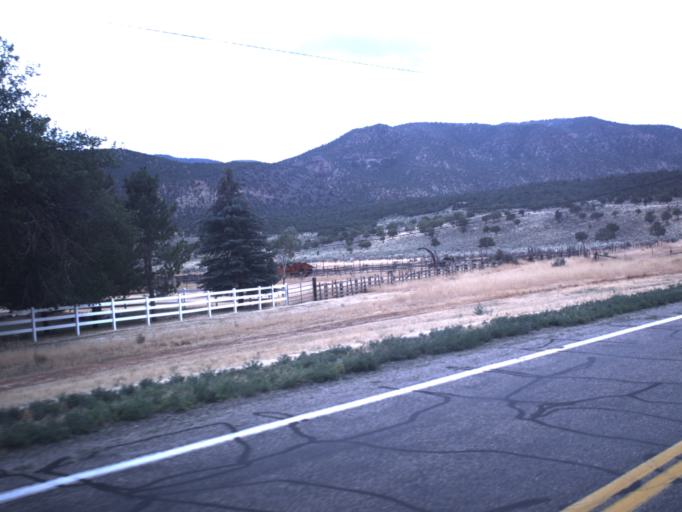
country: US
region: Utah
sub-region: Iron County
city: Parowan
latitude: 37.8831
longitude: -112.7751
